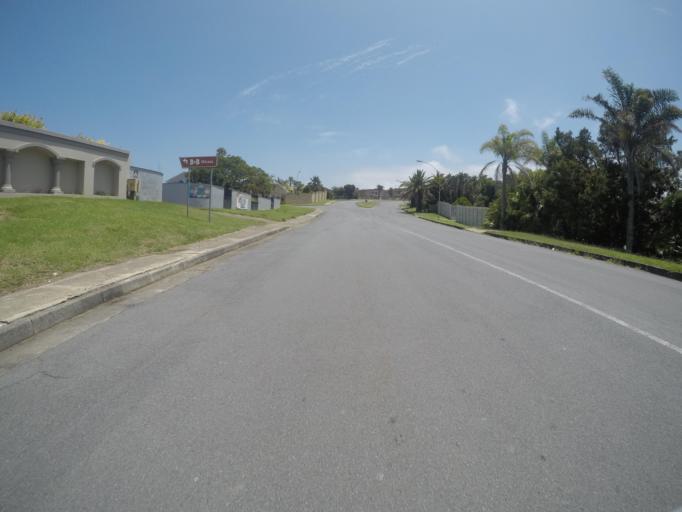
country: ZA
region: Eastern Cape
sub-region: Buffalo City Metropolitan Municipality
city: East London
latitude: -33.0027
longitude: 27.9231
